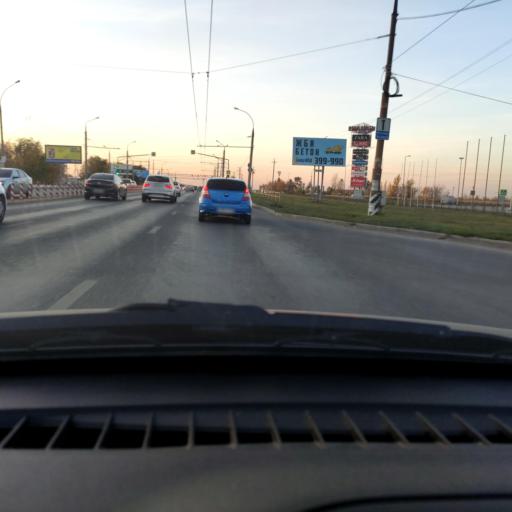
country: RU
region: Samara
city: Tol'yatti
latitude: 53.5425
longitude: 49.3846
